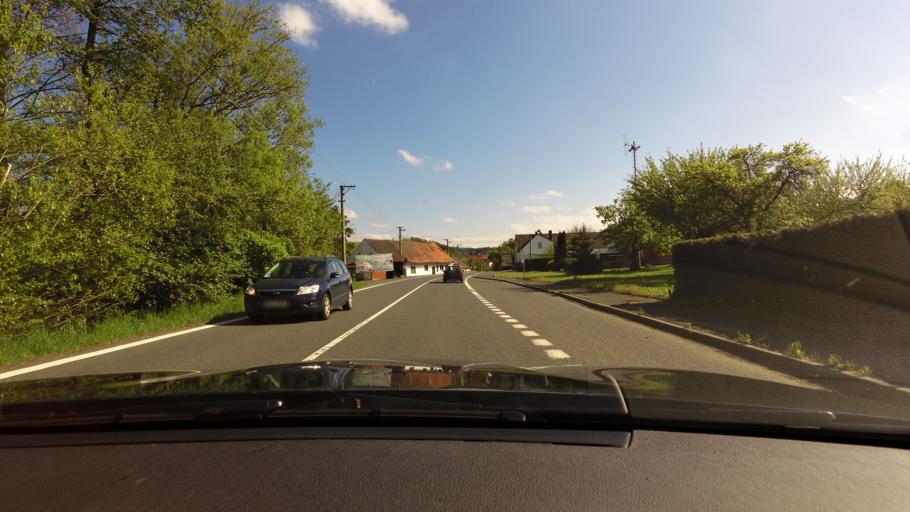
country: CZ
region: Plzensky
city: Strazov
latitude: 49.3287
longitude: 13.3023
